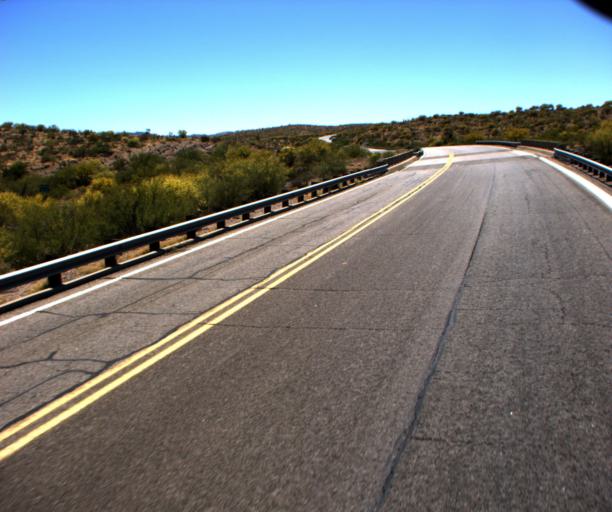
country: US
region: Arizona
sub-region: Pinal County
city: Mammoth
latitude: 32.6644
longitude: -110.6825
